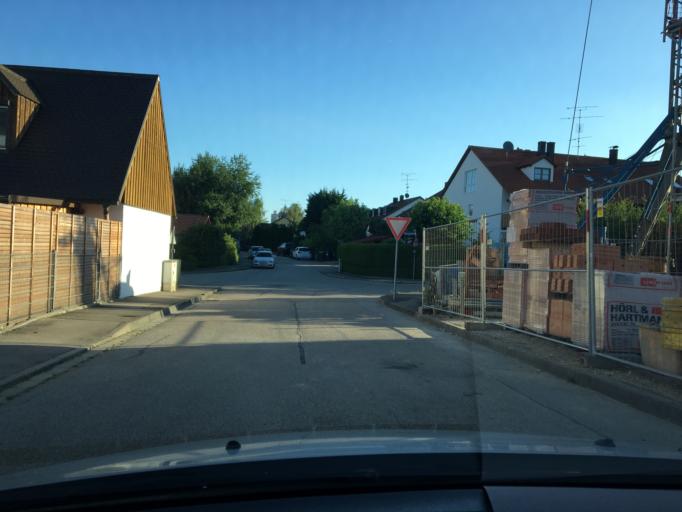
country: DE
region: Bavaria
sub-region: Upper Bavaria
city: Haimhausen
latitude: 48.3129
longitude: 11.5570
